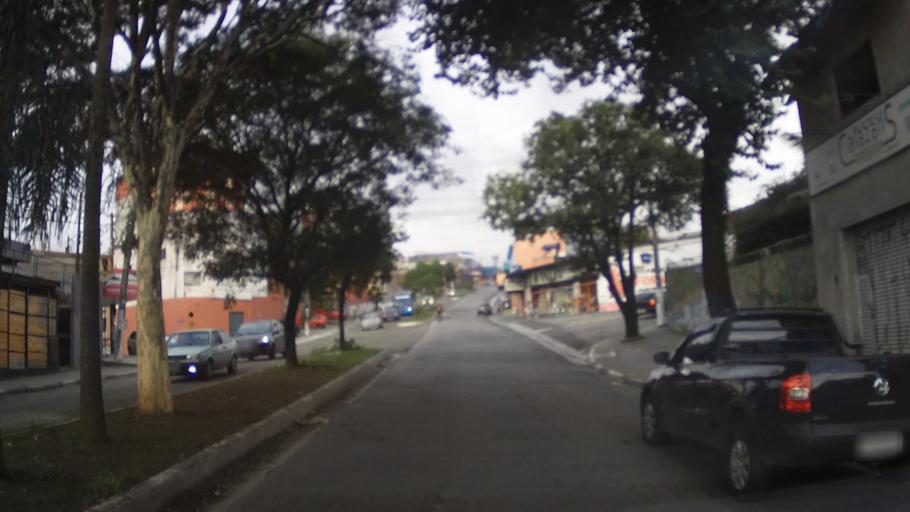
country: BR
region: Sao Paulo
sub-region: Itaquaquecetuba
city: Itaquaquecetuba
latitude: -23.4463
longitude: -46.4174
